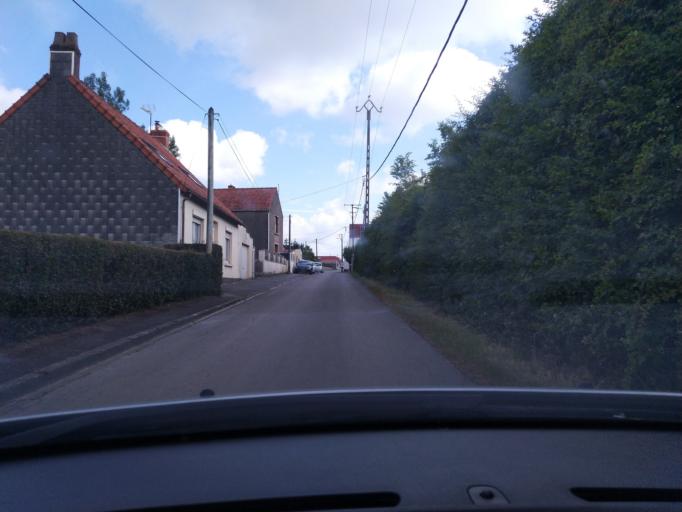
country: FR
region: Nord-Pas-de-Calais
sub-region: Departement du Pas-de-Calais
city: Ferques
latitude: 50.8374
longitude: 1.7544
